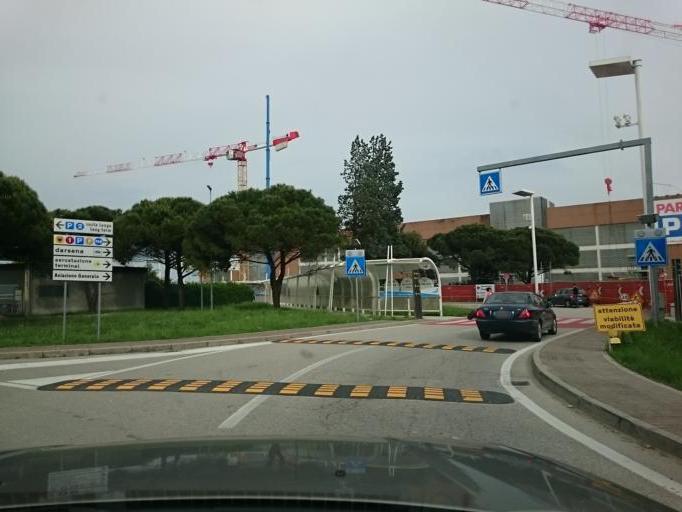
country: IT
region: Veneto
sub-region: Provincia di Venezia
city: Tessera
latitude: 45.5028
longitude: 12.3364
